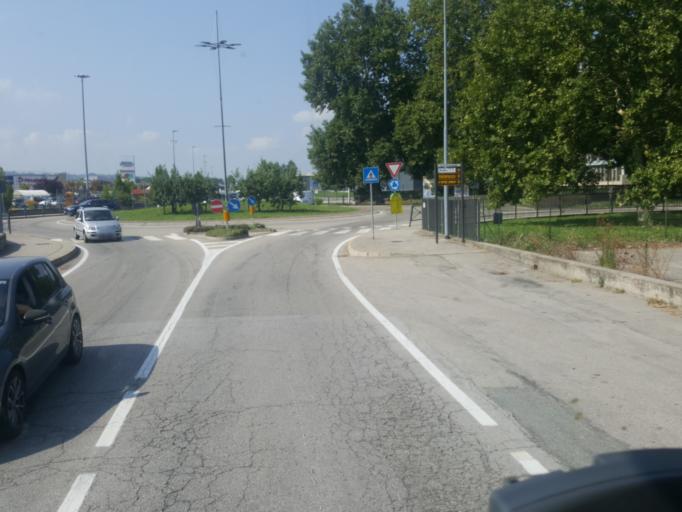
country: IT
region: Piedmont
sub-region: Provincia di Cuneo
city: Mussotto
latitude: 44.7188
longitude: 8.0354
